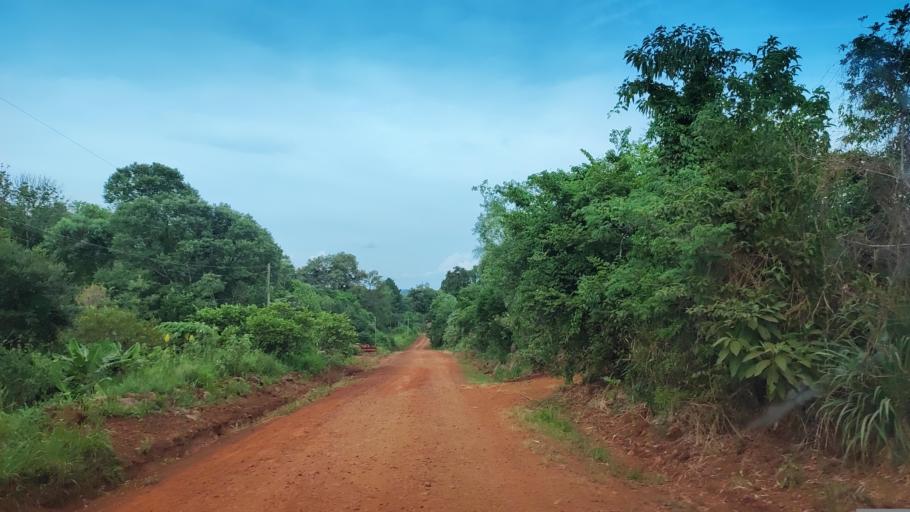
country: AR
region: Misiones
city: Gobernador Roca
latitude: -27.1496
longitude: -55.4815
